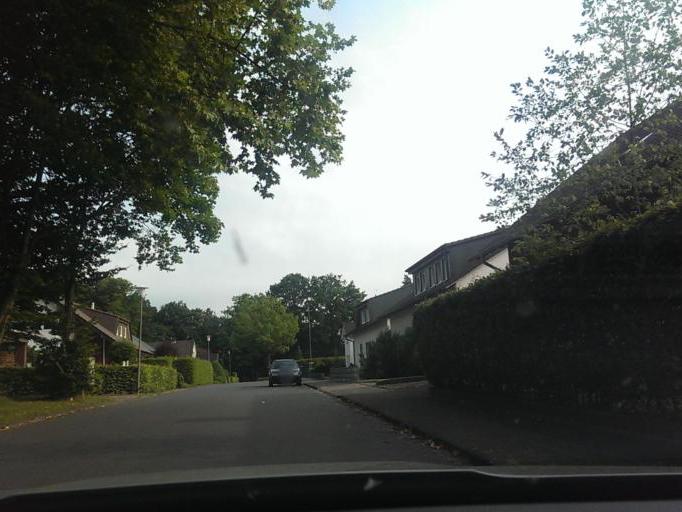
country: DE
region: North Rhine-Westphalia
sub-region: Regierungsbezirk Detmold
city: Delbruck
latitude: 51.7668
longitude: 8.5712
